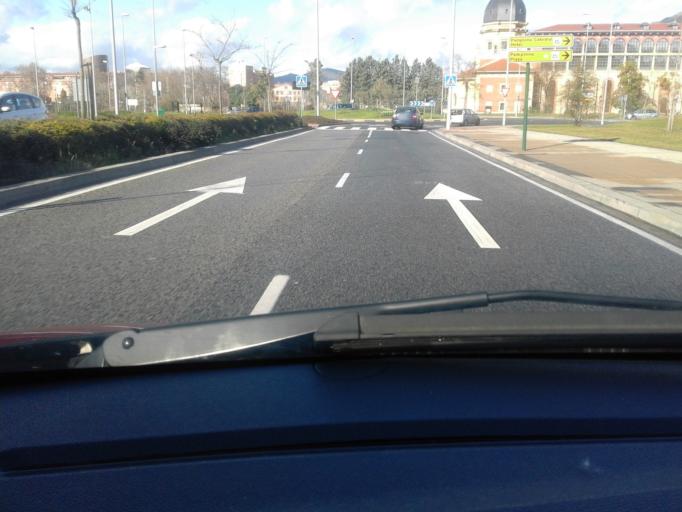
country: ES
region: Navarre
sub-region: Provincia de Navarra
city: Primer Ensanche
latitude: 42.8209
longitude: -1.6556
